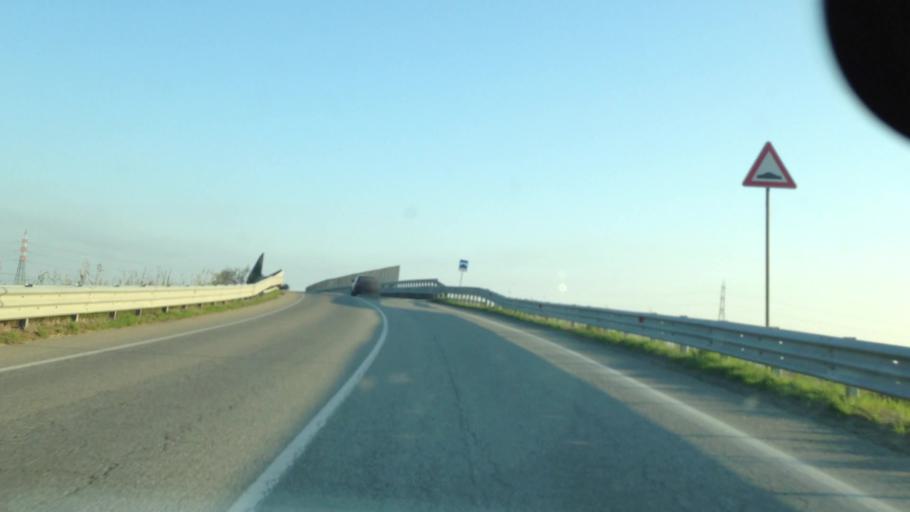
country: IT
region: Piedmont
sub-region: Provincia di Vercelli
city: Cigliano
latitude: 45.2966
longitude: 8.0435
